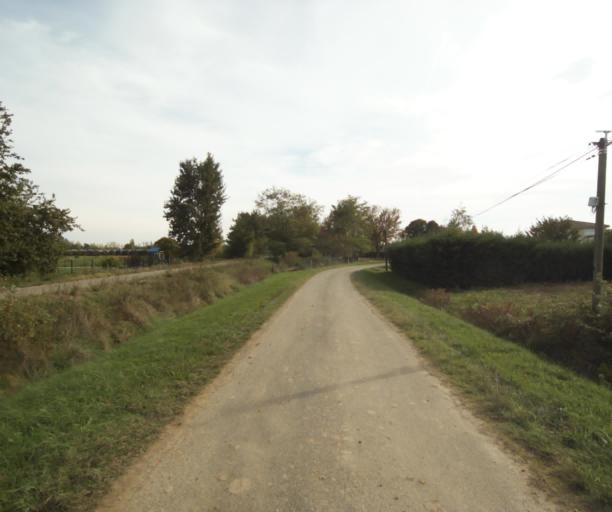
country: FR
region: Midi-Pyrenees
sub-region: Departement du Tarn-et-Garonne
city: Labastide-Saint-Pierre
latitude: 43.9290
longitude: 1.3545
